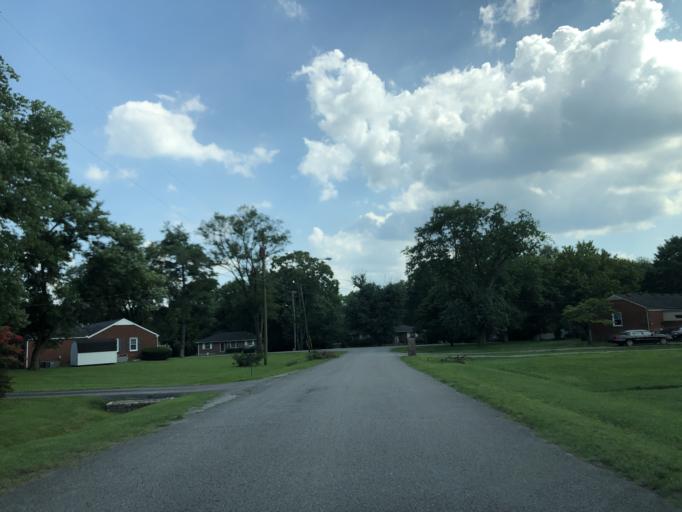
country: US
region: Tennessee
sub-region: Davidson County
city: Oak Hill
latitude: 36.1201
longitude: -86.7217
